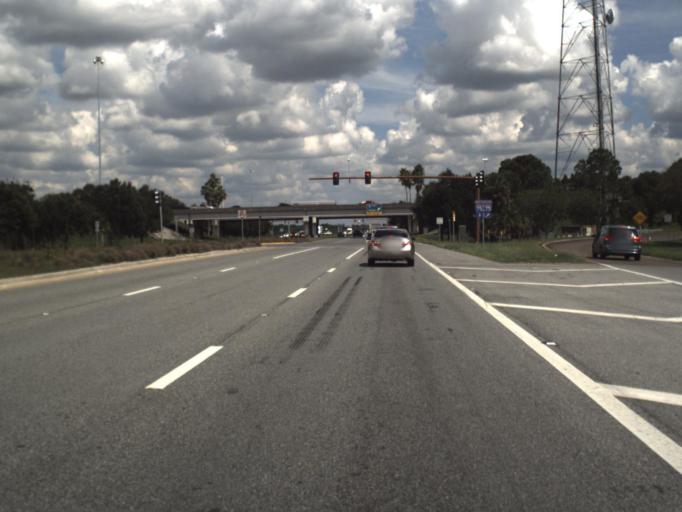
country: US
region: Florida
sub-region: Sarasota County
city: Fruitville
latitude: 27.3381
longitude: -82.4493
